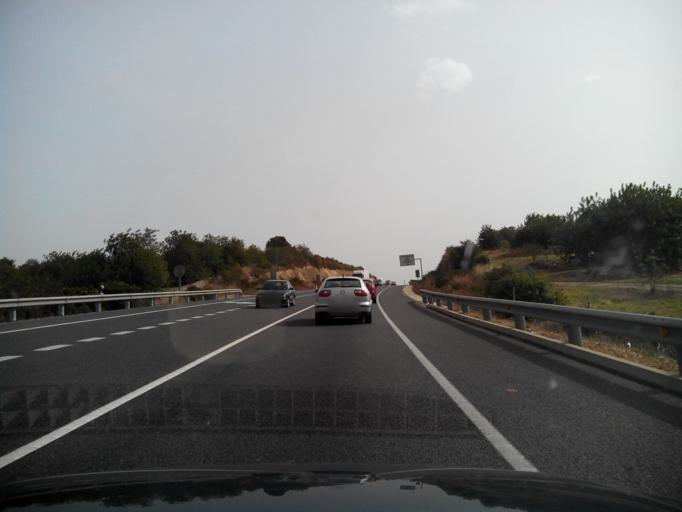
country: ES
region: Catalonia
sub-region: Provincia de Tarragona
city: Torredembarra
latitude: 41.1623
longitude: 1.4086
